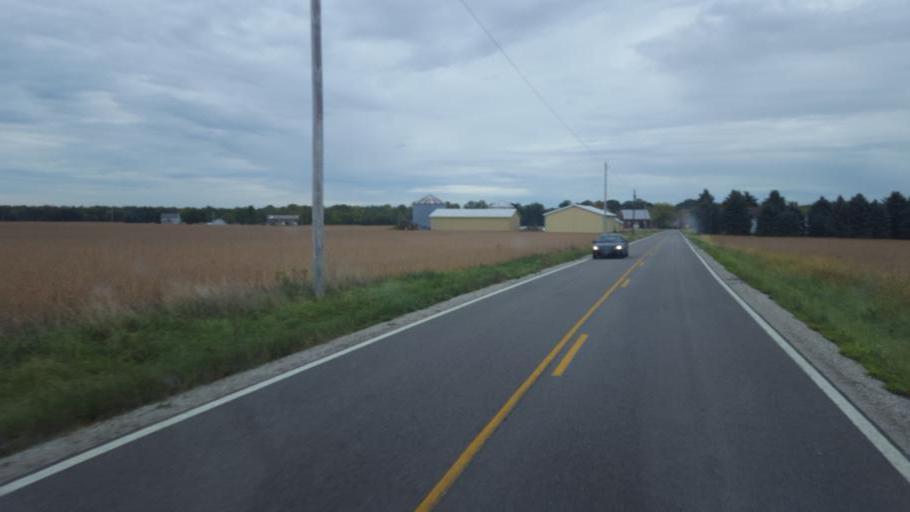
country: US
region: Ohio
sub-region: Huron County
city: New London
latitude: 41.1397
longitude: -82.4148
